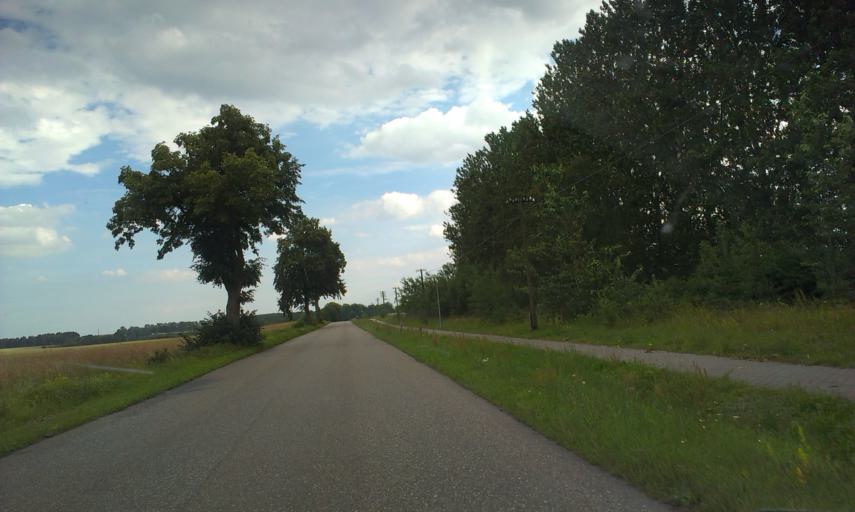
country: PL
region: Greater Poland Voivodeship
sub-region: Powiat zlotowski
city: Zlotow
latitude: 53.4040
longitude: 16.9928
